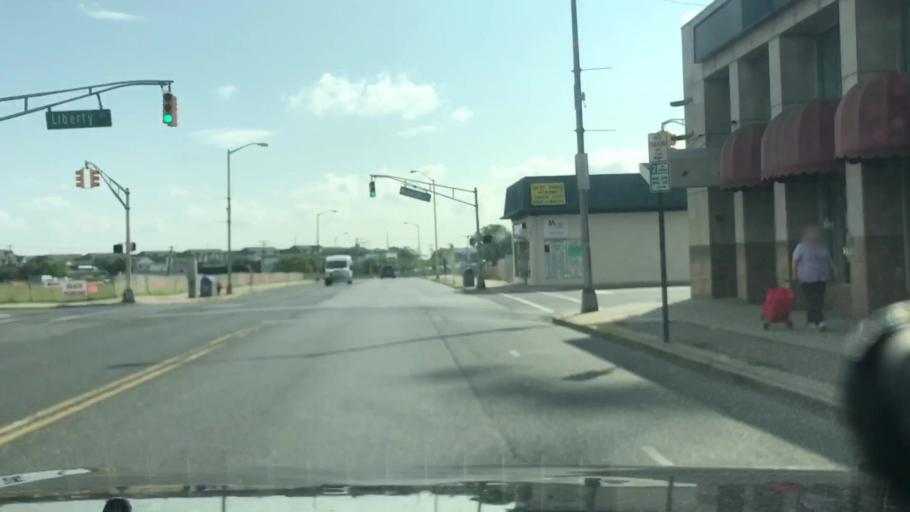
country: US
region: New Jersey
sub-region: Monmouth County
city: Long Branch
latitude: 40.3046
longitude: -73.9861
